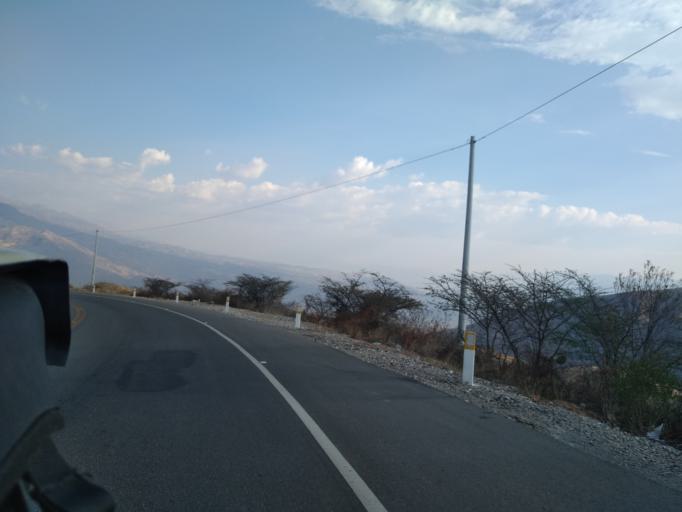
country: PE
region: Cajamarca
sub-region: San Marcos
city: La Grama
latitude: -7.4041
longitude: -78.1243
